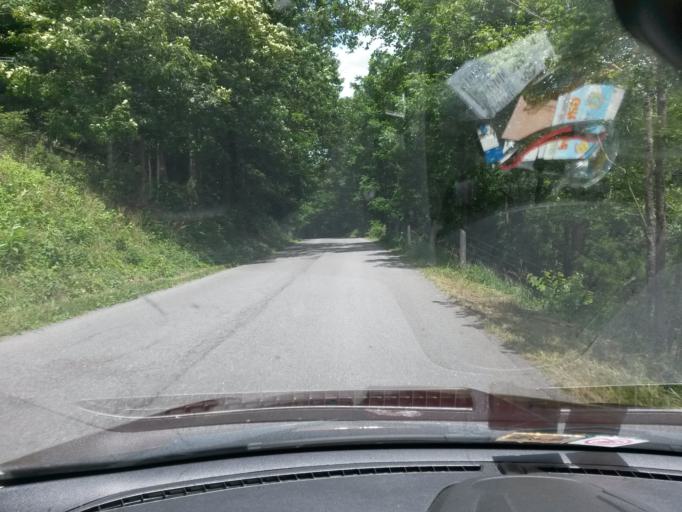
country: US
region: West Virginia
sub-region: Monroe County
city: Union
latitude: 37.5250
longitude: -80.5509
